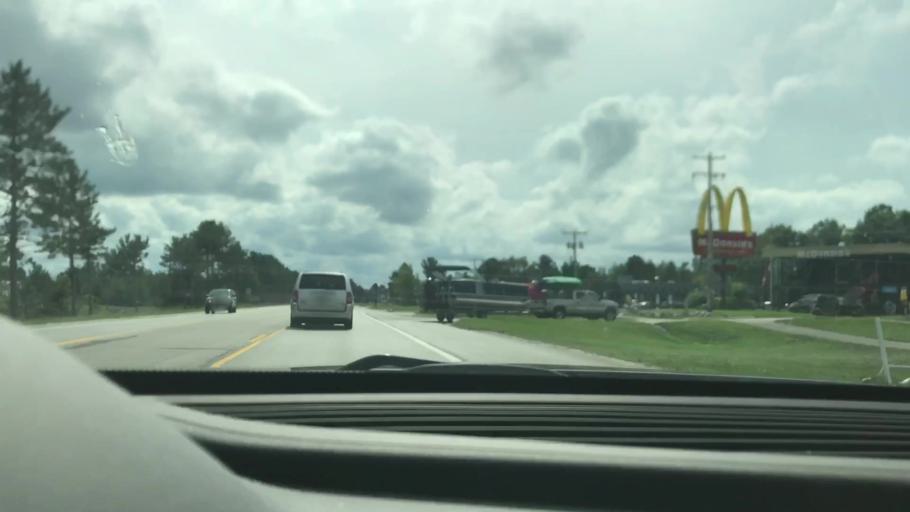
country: US
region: Michigan
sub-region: Kalkaska County
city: Kalkaska
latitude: 44.7257
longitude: -85.1829
